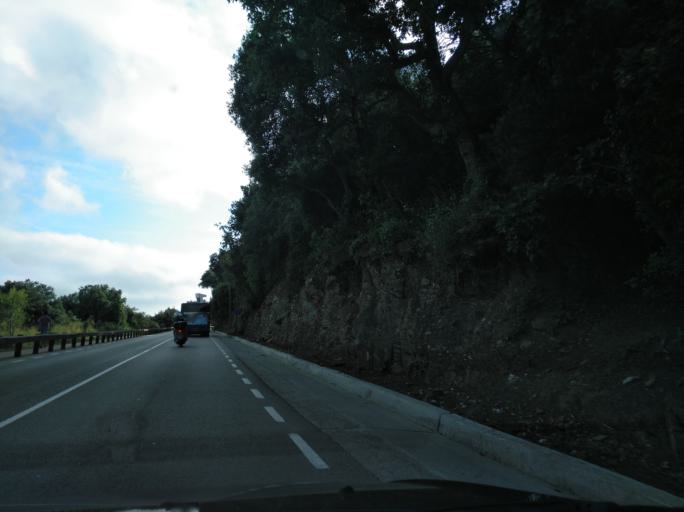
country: ES
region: Catalonia
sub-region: Provincia de Barcelona
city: Sarria-Sant Gervasi
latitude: 41.4263
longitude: 2.1229
